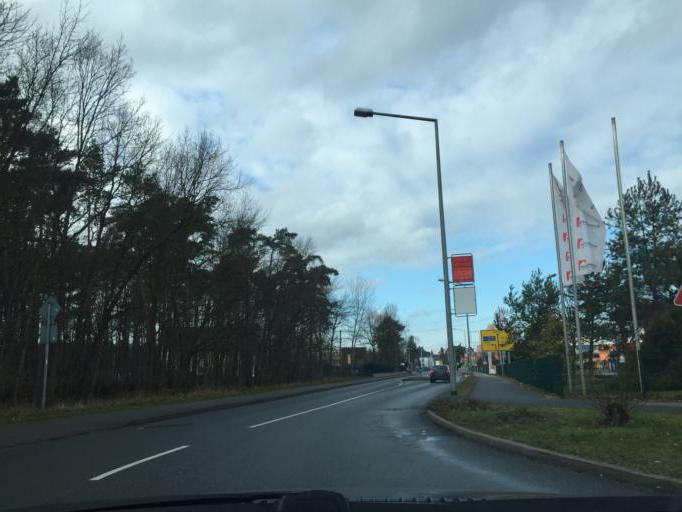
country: DE
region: Saxony
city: Ottendorf-Okrilla
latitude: 51.1754
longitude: 13.8274
